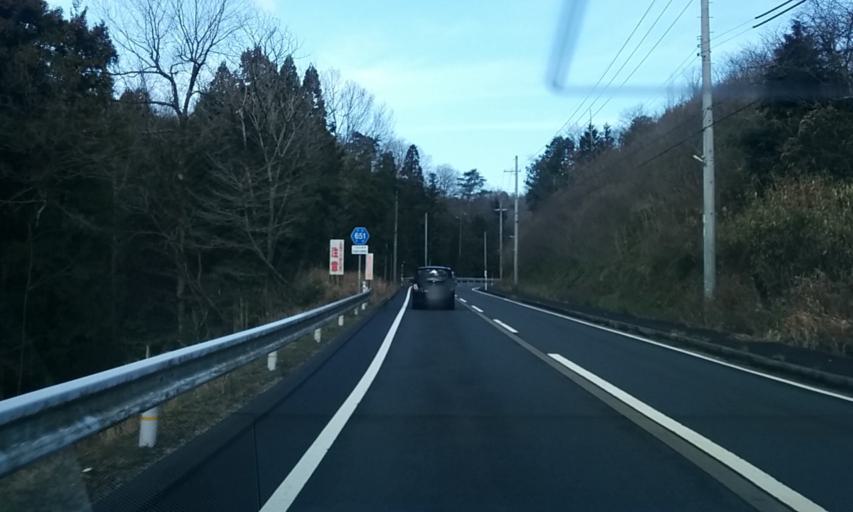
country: JP
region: Kyoto
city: Miyazu
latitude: 35.5796
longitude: 135.1192
